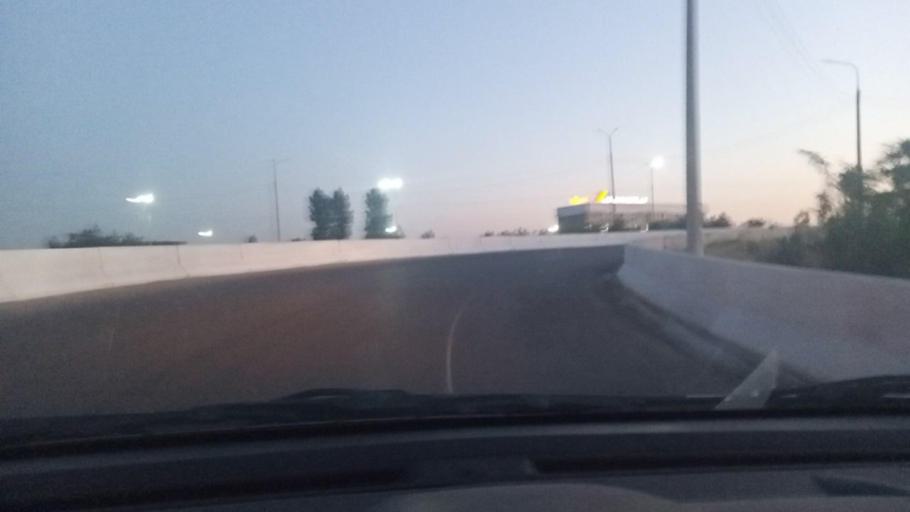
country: UZ
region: Toshkent Shahri
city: Tashkent
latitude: 41.2423
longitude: 69.2160
